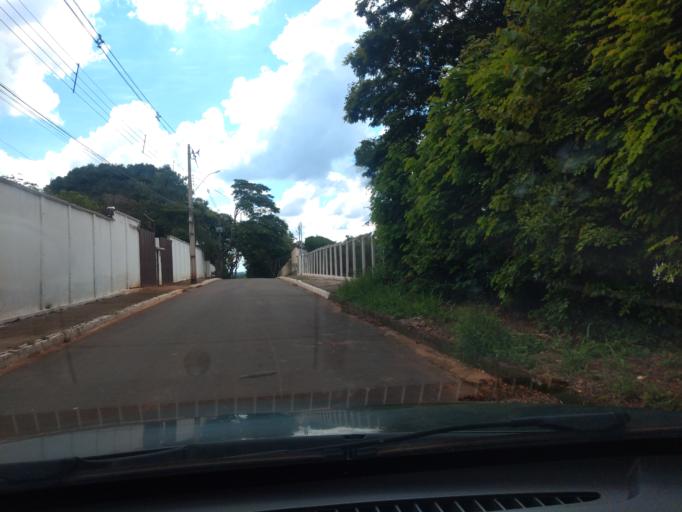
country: BR
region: Minas Gerais
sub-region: Tres Coracoes
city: Tres Coracoes
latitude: -21.6880
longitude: -45.2692
